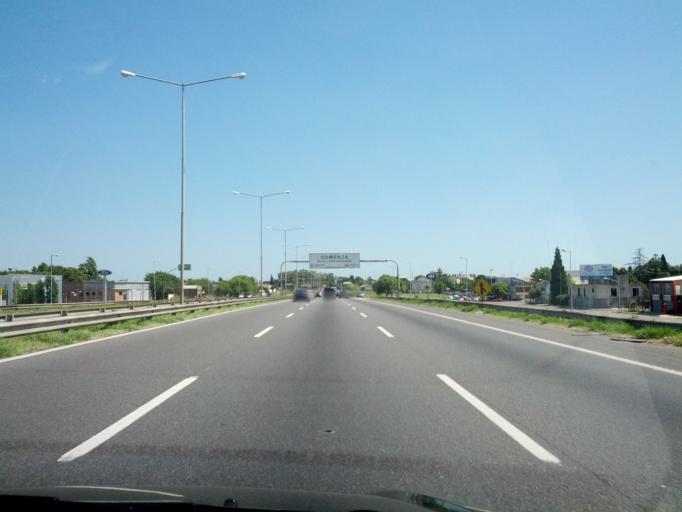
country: AR
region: Buenos Aires
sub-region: Partido de Campana
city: Campana
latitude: -34.1895
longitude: -58.9444
